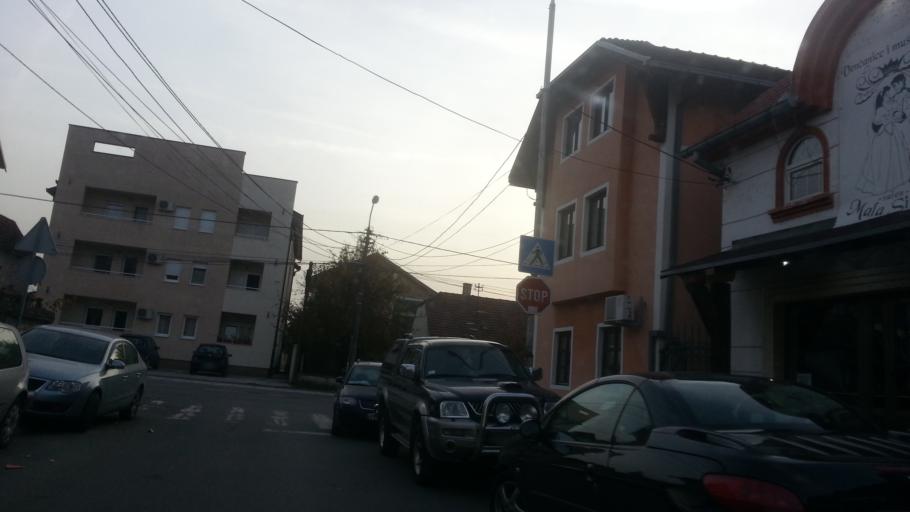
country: RS
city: Novi Banovci
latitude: 44.8994
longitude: 20.2811
